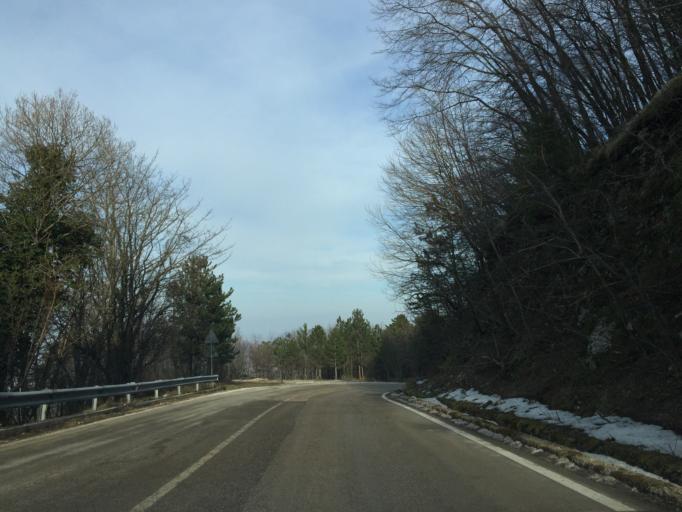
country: IT
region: Molise
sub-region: Provincia di Campobasso
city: San Massimo
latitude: 41.4767
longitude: 14.4120
